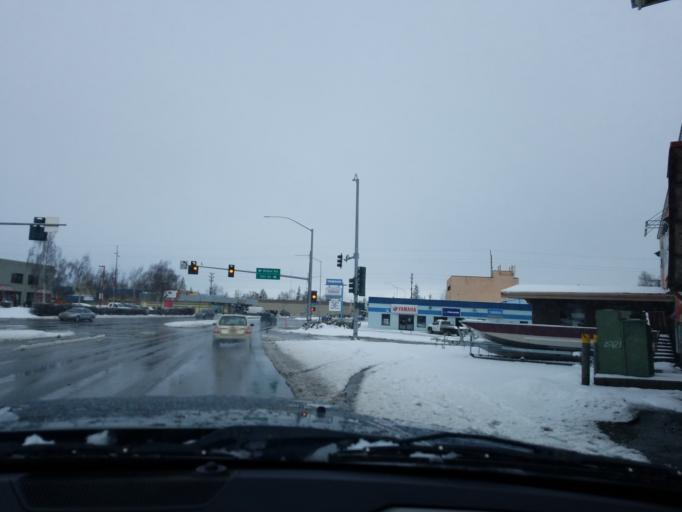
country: US
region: Alaska
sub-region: Anchorage Municipality
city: Anchorage
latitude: 61.1849
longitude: -149.9240
